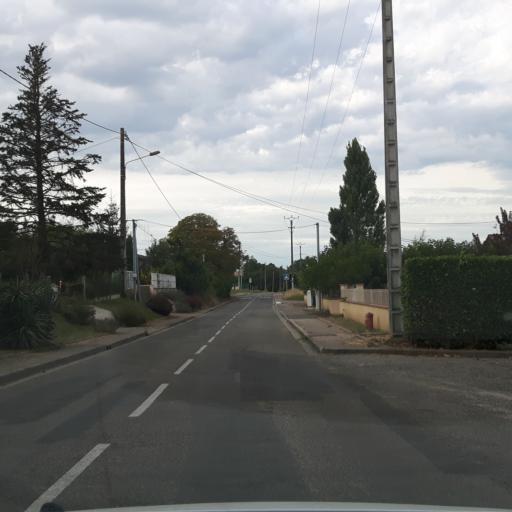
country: FR
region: Midi-Pyrenees
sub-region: Departement de la Haute-Garonne
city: Fronton
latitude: 43.8381
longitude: 1.3832
